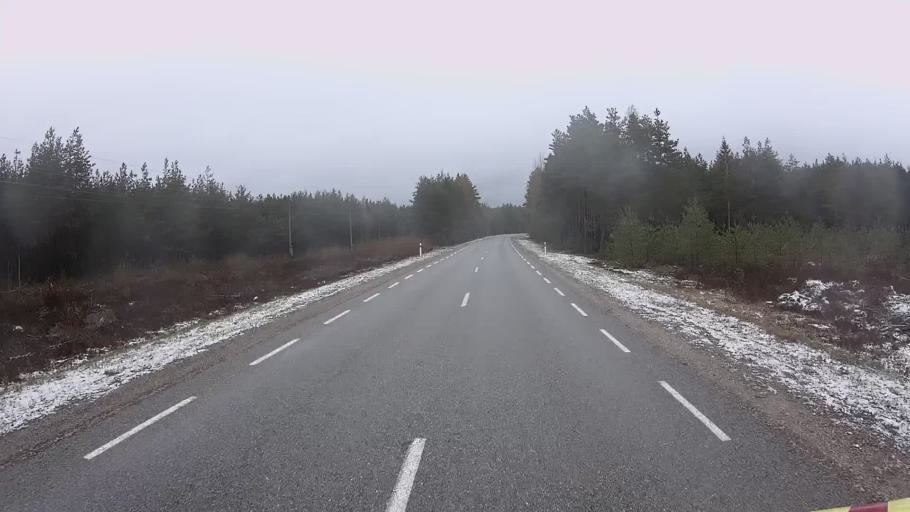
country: EE
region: Hiiumaa
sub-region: Kaerdla linn
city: Kardla
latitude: 59.0259
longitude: 22.6719
